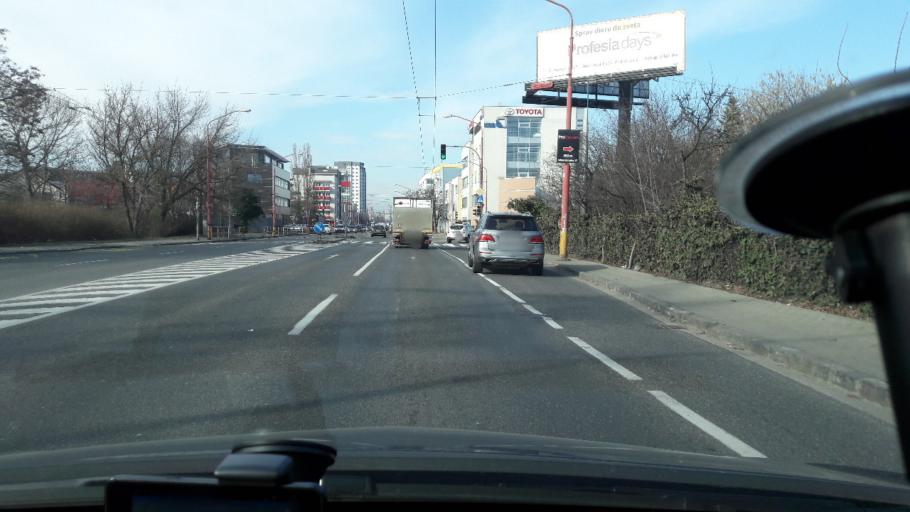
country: SK
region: Bratislavsky
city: Bratislava
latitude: 48.1509
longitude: 17.1764
